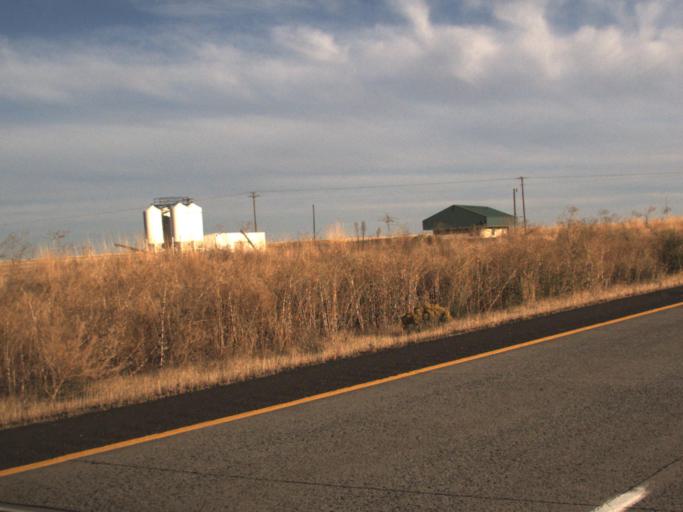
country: US
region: Washington
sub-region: Franklin County
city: Connell
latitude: 46.7195
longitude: -118.8347
